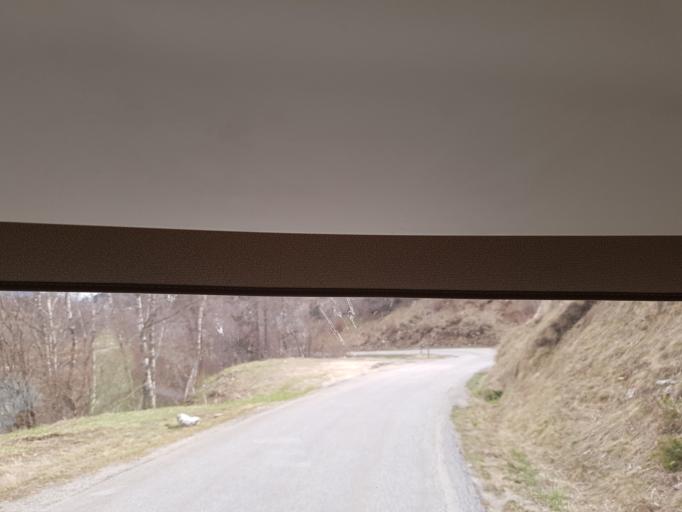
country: FR
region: Languedoc-Roussillon
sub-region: Departement de l'Aude
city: Quillan
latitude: 42.6620
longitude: 2.1256
